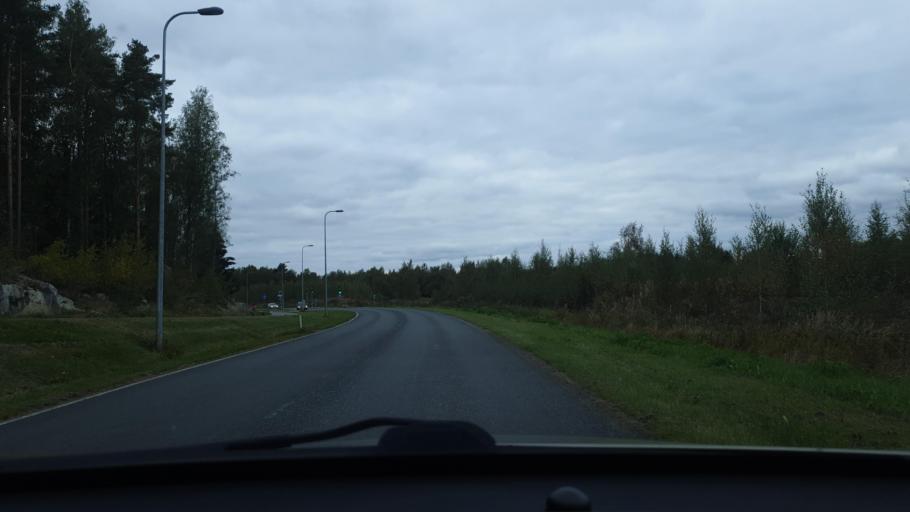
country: FI
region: Ostrobothnia
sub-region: Vaasa
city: Teeriniemi
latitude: 63.0994
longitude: 21.6969
